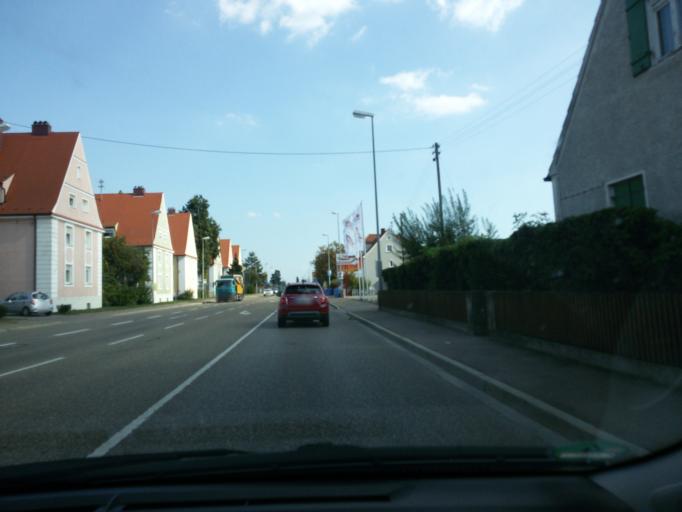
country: DE
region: Bavaria
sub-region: Swabia
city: Noerdlingen
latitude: 48.8461
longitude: 10.4982
